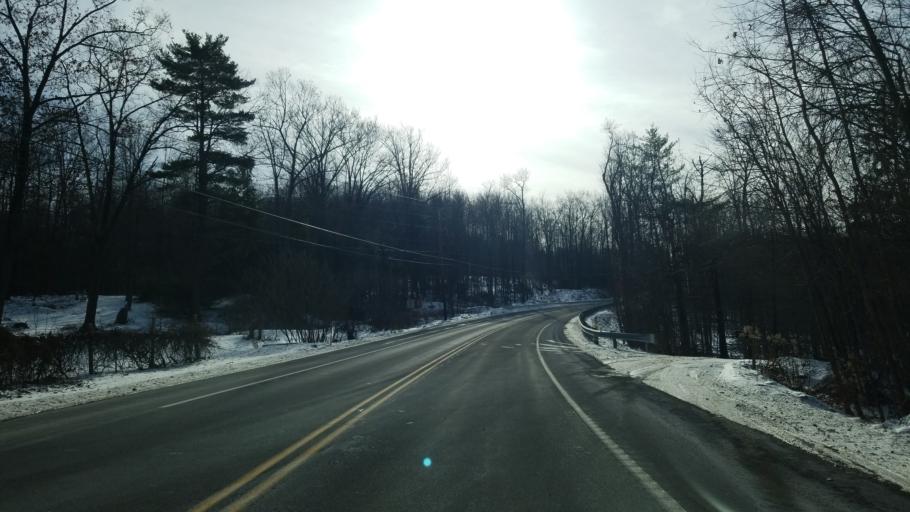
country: US
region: Pennsylvania
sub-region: Clearfield County
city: Treasure Lake
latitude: 41.1615
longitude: -78.5484
